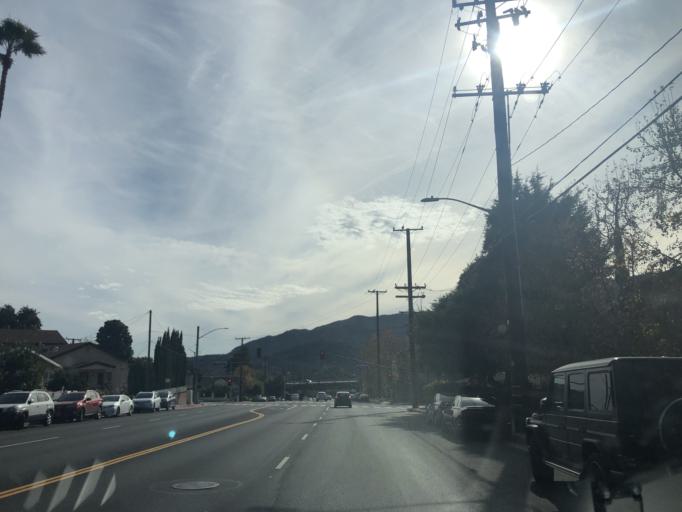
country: US
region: California
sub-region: Los Angeles County
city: La Crescenta-Montrose
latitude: 34.2260
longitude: -118.2485
